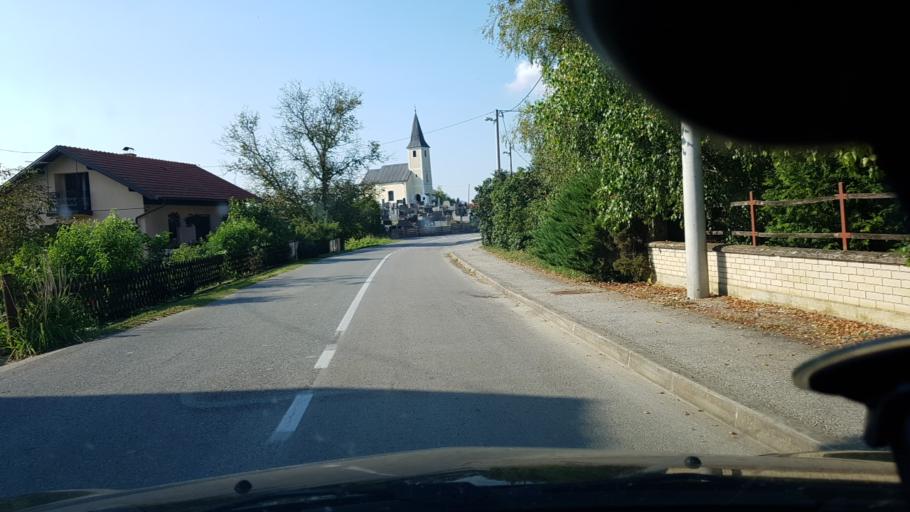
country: HR
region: Zagrebacka
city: Pojatno
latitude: 45.9502
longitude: 15.7327
